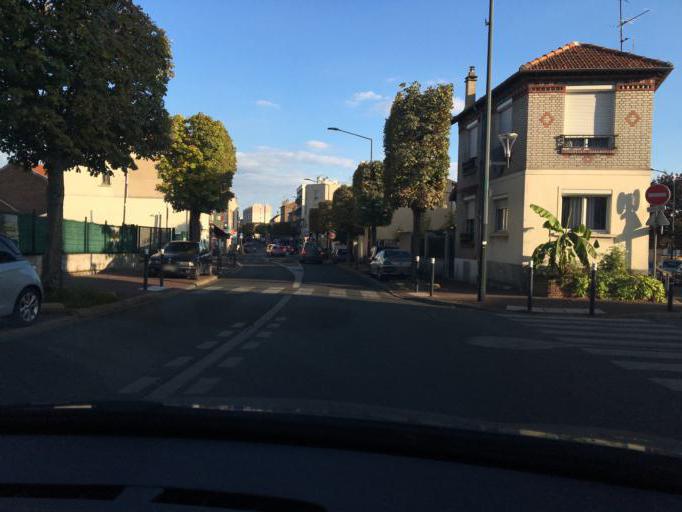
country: FR
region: Ile-de-France
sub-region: Departement du Val-de-Marne
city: Fontenay-sous-Bois
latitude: 48.8545
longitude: 2.4686
